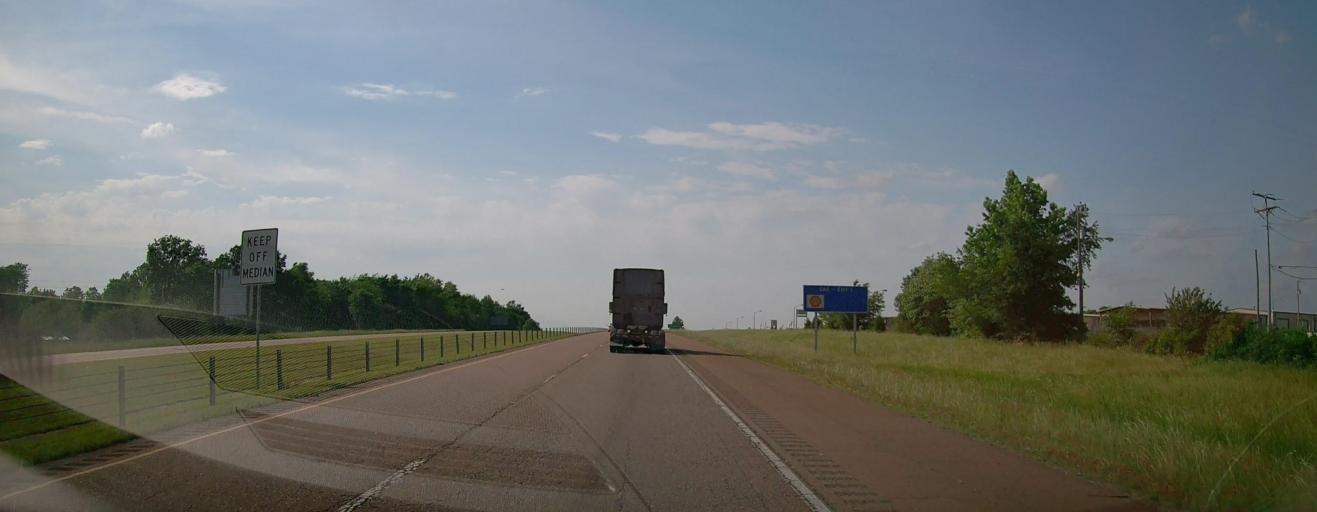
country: US
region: Mississippi
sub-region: De Soto County
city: Olive Branch
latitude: 34.9712
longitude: -89.8600
